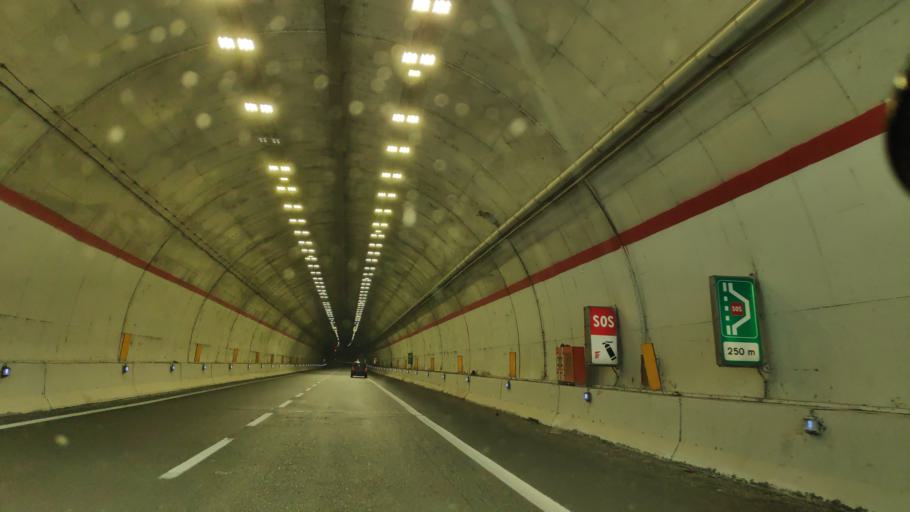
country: IT
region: Campania
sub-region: Provincia di Salerno
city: Sicignano degli Alburni
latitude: 40.6048
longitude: 15.3007
